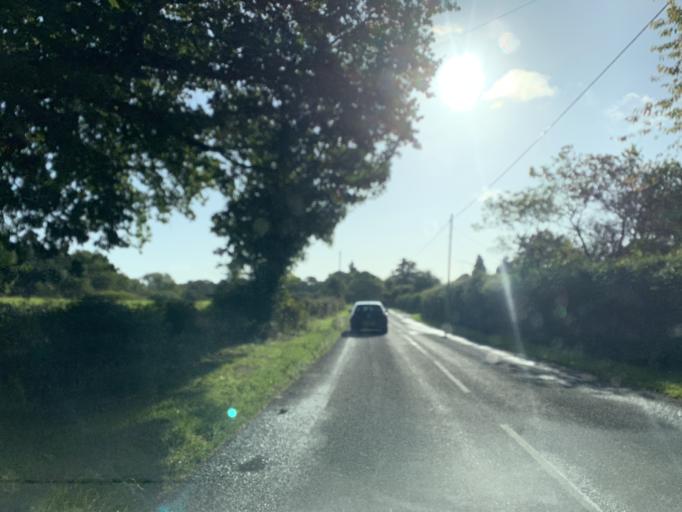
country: GB
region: England
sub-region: Wiltshire
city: Downton
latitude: 50.9741
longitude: -1.7164
